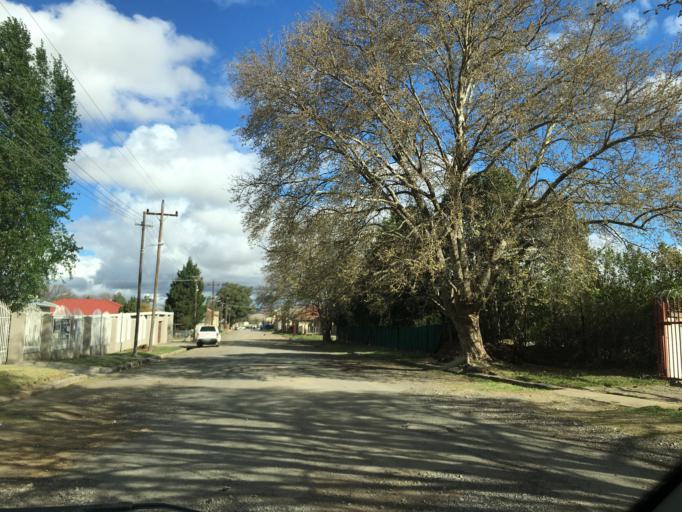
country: ZA
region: Eastern Cape
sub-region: Chris Hani District Municipality
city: Elliot
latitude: -31.3307
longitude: 27.8508
